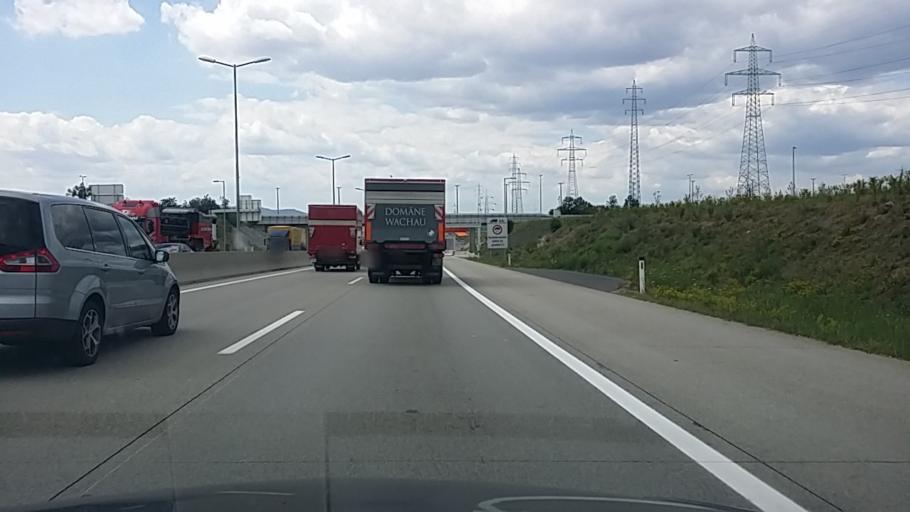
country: AT
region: Lower Austria
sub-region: Politischer Bezirk Modling
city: Hennersdorf
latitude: 48.1275
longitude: 16.3734
